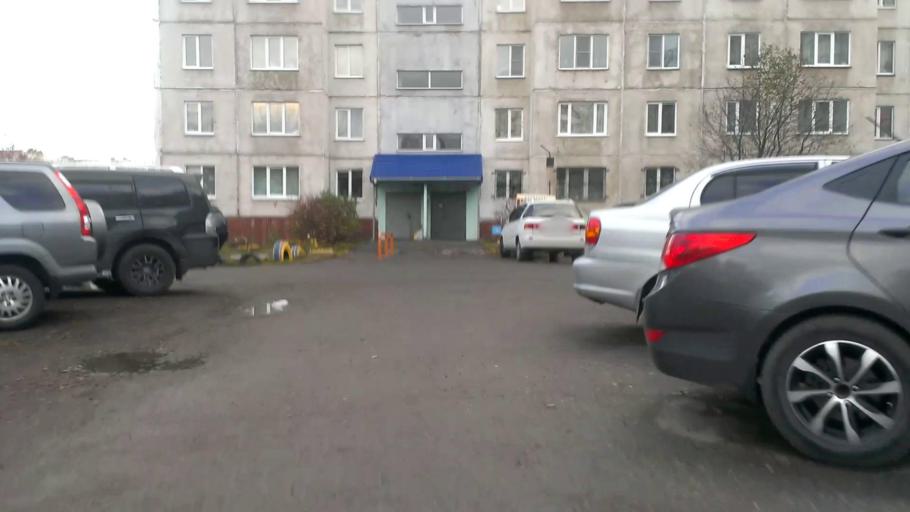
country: RU
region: Altai Krai
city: Novosilikatnyy
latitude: 53.3591
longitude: 83.6762
